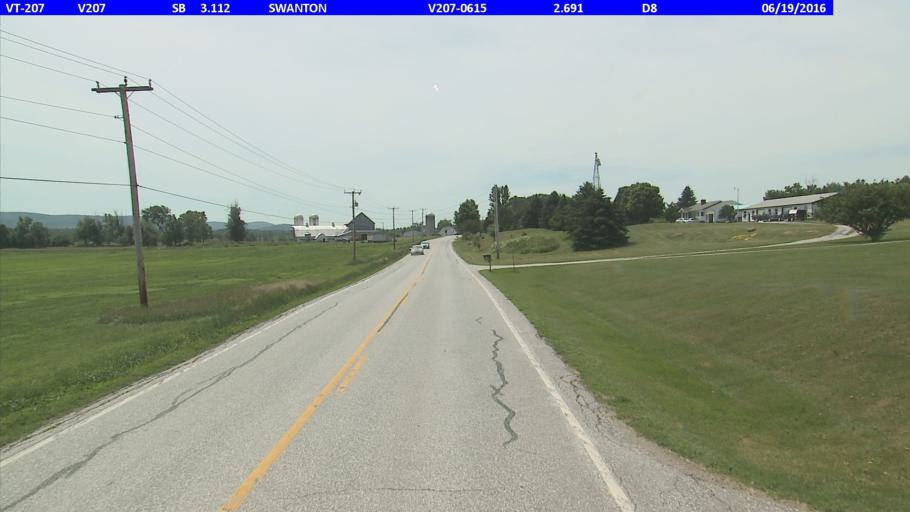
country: US
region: Vermont
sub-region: Franklin County
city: Swanton
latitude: 44.8829
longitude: -73.0685
